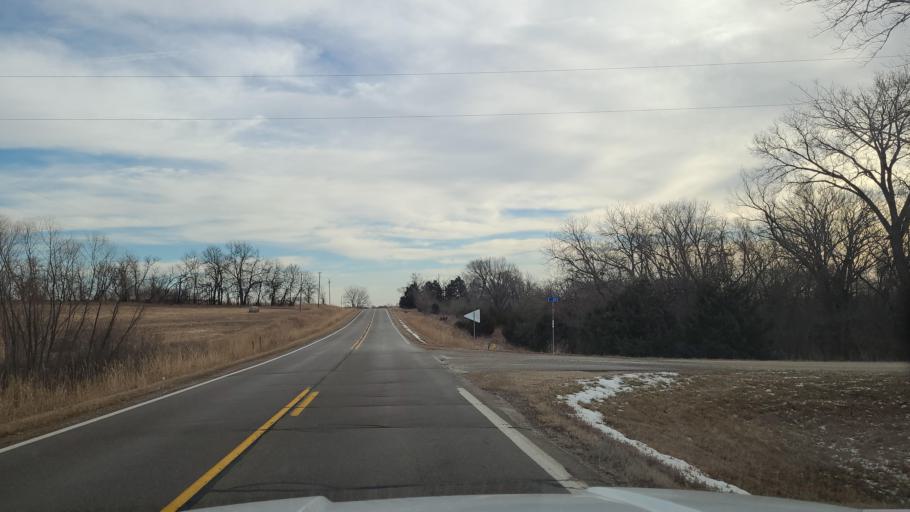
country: US
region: Kansas
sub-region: Douglas County
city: Lawrence
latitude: 39.0437
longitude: -95.4242
